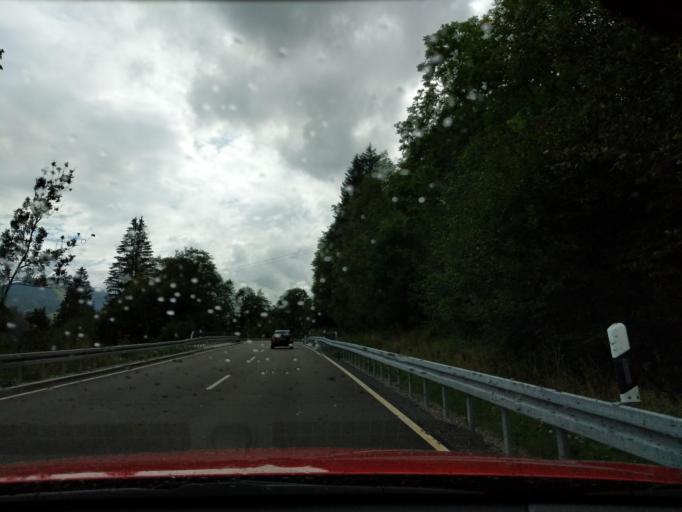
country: DE
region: Bavaria
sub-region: Swabia
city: Oberstaufen
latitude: 47.5504
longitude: 10.0391
